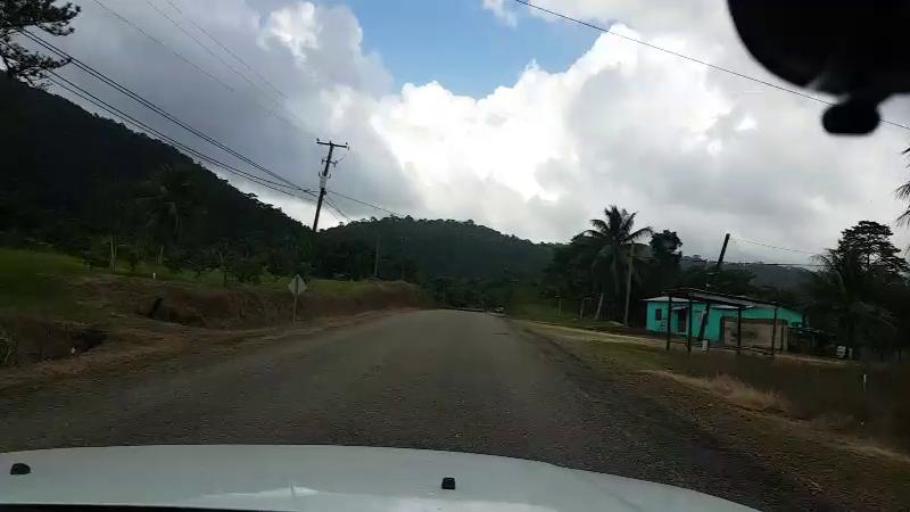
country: BZ
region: Stann Creek
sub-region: Dangriga
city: Dangriga
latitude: 17.0012
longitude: -88.4422
